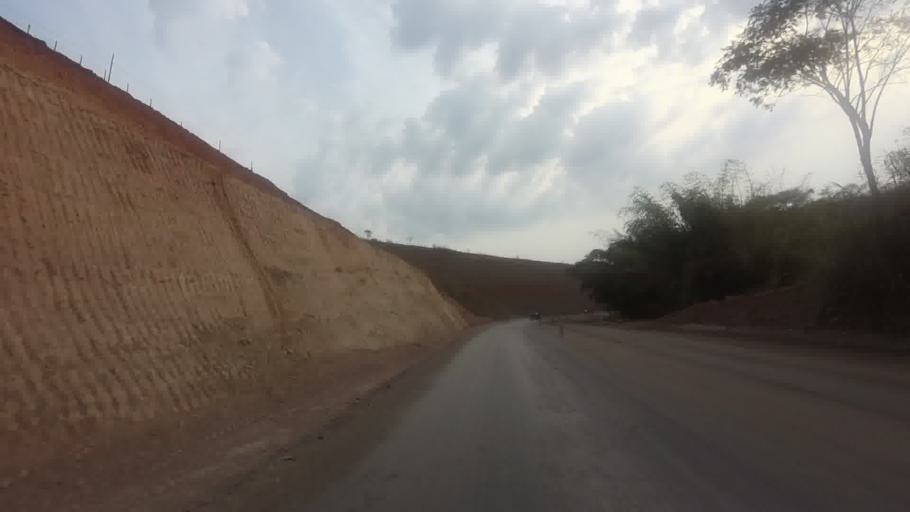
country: BR
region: Rio de Janeiro
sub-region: Santo Antonio De Padua
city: Santo Antonio de Padua
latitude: -21.5097
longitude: -42.0880
